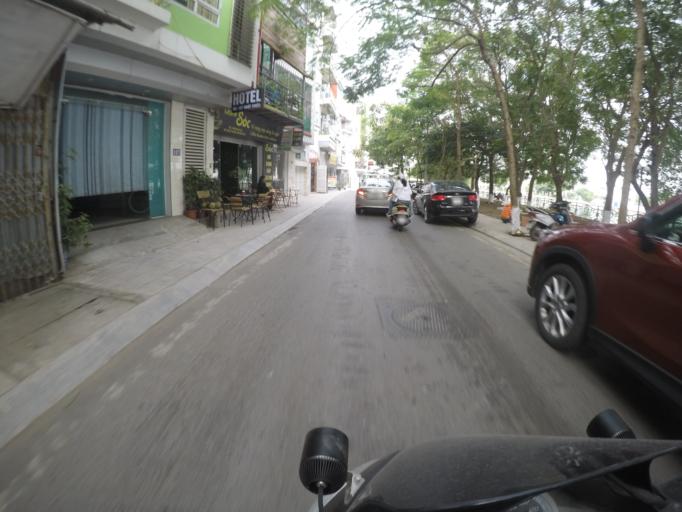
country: VN
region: Ha Noi
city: Tay Ho
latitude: 21.0724
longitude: 105.8145
